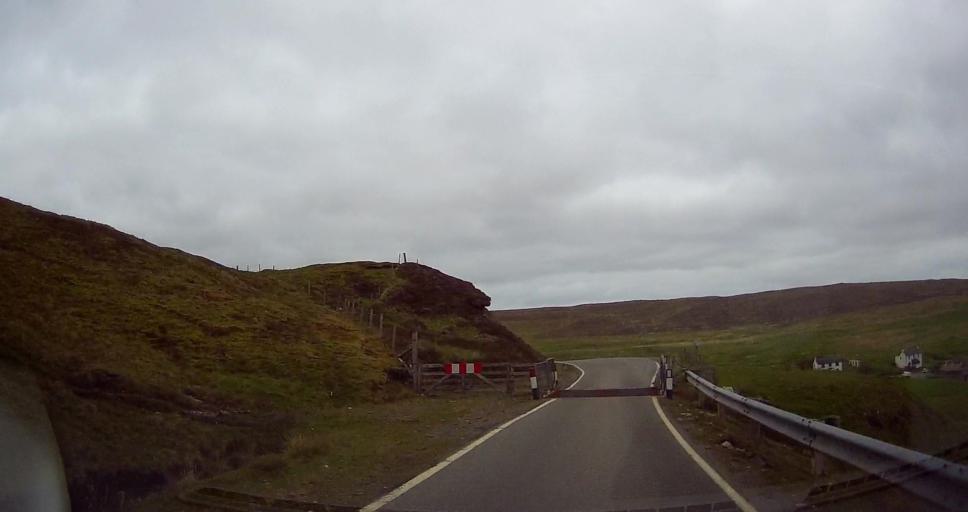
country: GB
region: Scotland
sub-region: Shetland Islands
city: Lerwick
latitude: 60.3429
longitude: -1.2843
